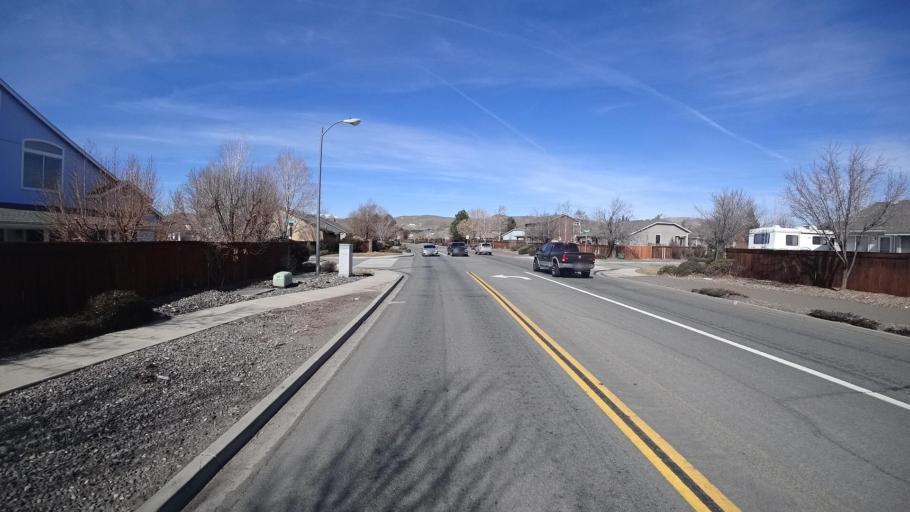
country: US
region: Nevada
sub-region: Washoe County
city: Sun Valley
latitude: 39.5875
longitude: -119.7191
